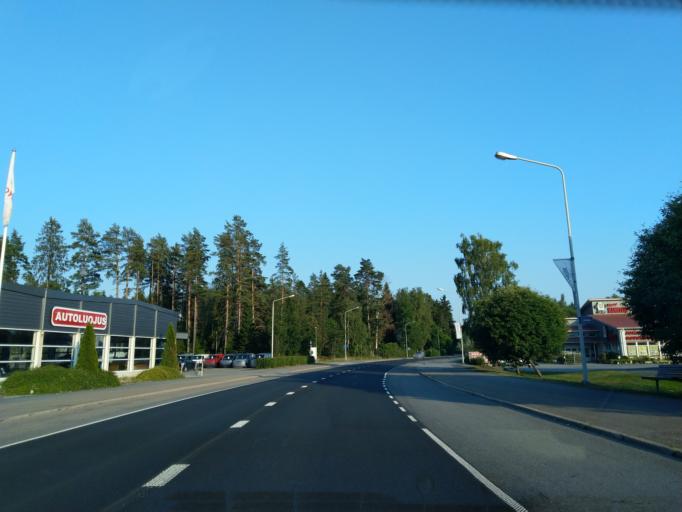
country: FI
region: Satakunta
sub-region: Pohjois-Satakunta
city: Kankaanpaeae
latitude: 61.8128
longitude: 22.3797
